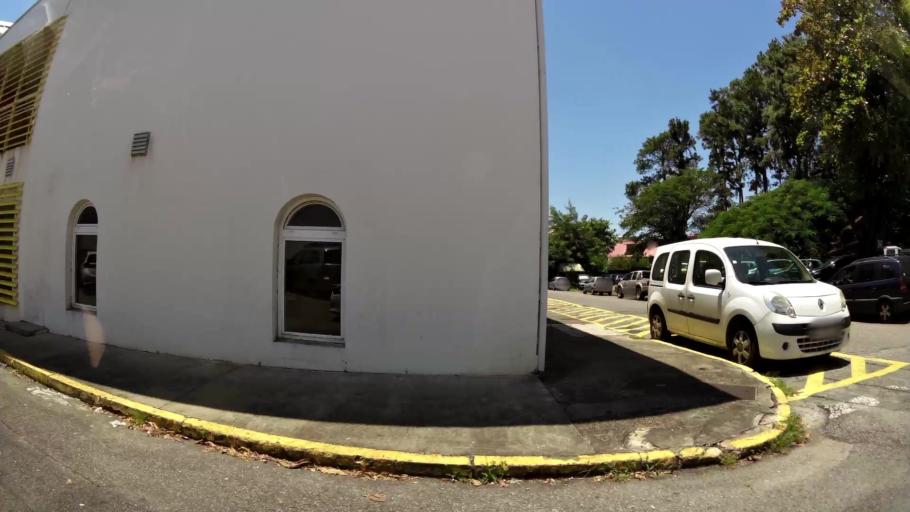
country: GF
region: Guyane
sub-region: Guyane
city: Cayenne
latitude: 4.9387
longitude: -52.3370
